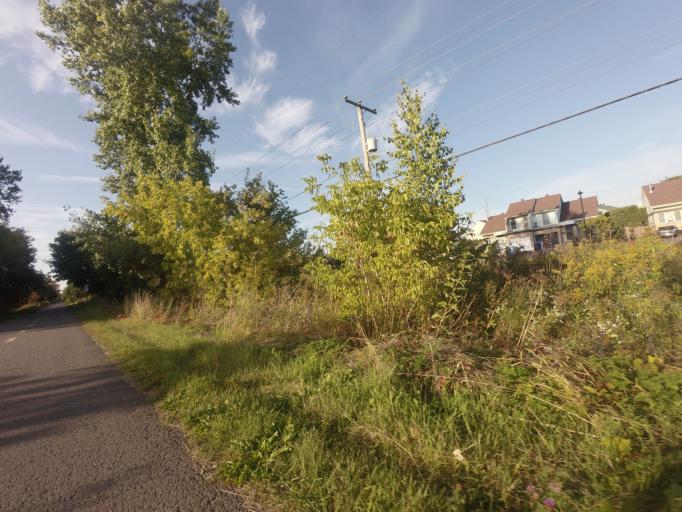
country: CA
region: Quebec
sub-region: Laurentides
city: Saint-Jerome
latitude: 45.7986
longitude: -74.0038
